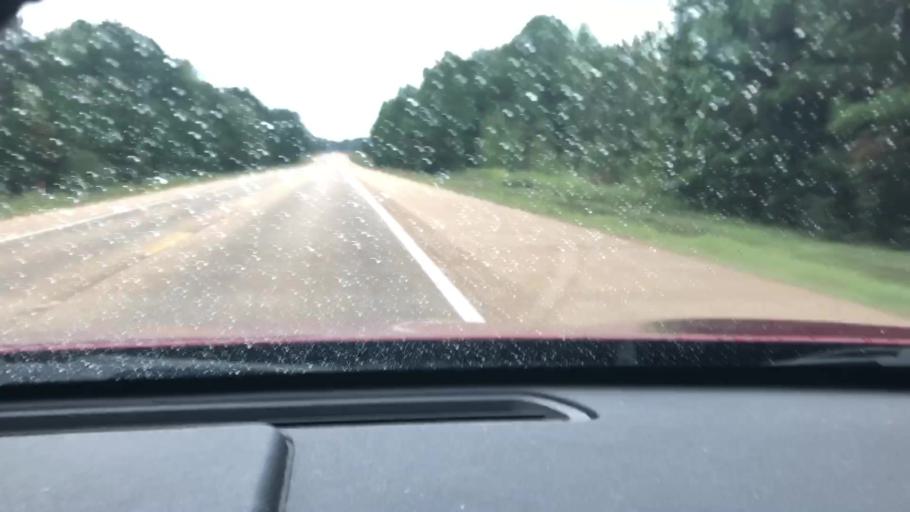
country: US
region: Arkansas
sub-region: Lafayette County
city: Stamps
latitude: 33.3590
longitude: -93.4174
